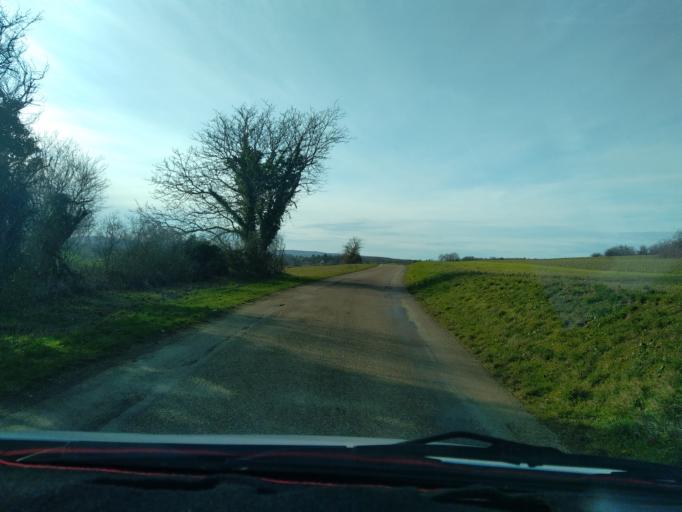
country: FR
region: Franche-Comte
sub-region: Departement de la Haute-Saone
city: Marnay
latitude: 47.3107
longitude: 5.6760
